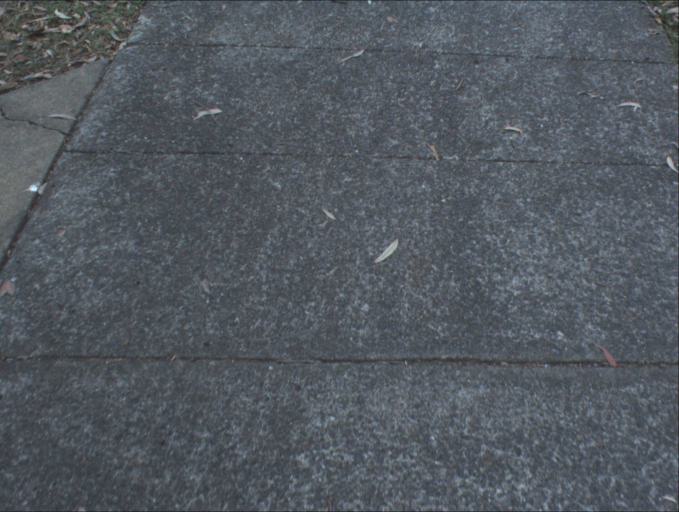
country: AU
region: Queensland
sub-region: Logan
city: Springwood
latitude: -27.6158
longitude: 153.1307
